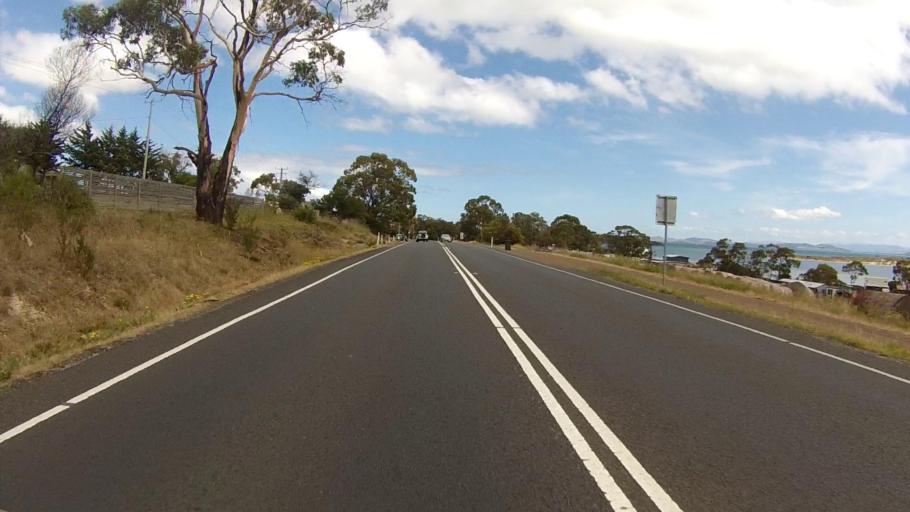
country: AU
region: Tasmania
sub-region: Sorell
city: Sorell
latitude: -42.8385
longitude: 147.6228
